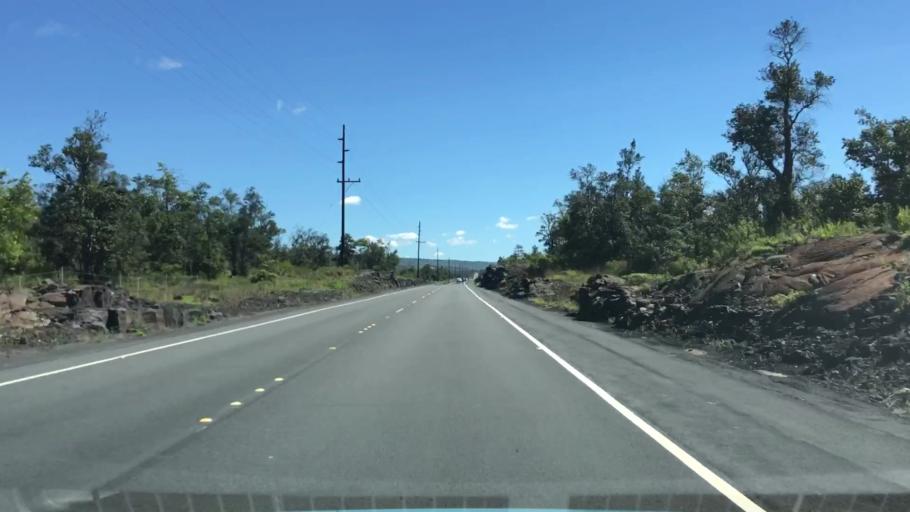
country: US
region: Hawaii
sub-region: Hawaii County
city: Pahala
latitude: 19.3031
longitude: -155.4159
